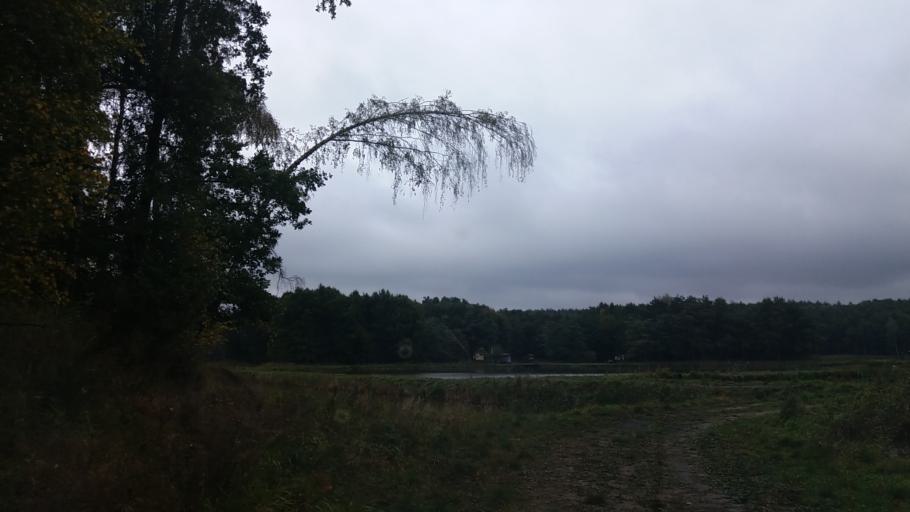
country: PL
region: West Pomeranian Voivodeship
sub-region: Powiat choszczenski
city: Pelczyce
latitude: 53.0681
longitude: 15.2823
